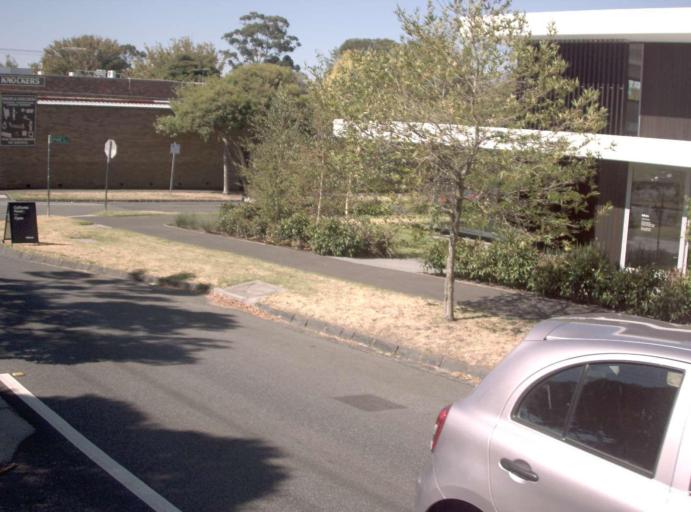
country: AU
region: Victoria
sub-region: Bayside
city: North Brighton
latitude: -37.9199
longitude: 145.0059
